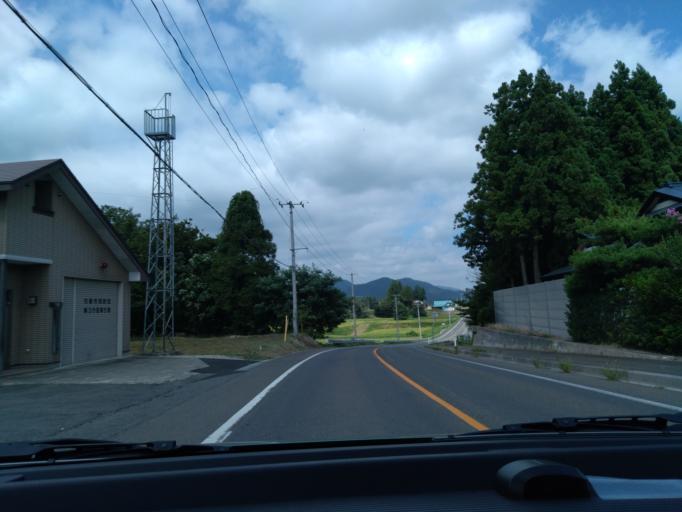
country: JP
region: Iwate
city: Hanamaki
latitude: 39.4193
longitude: 141.0757
